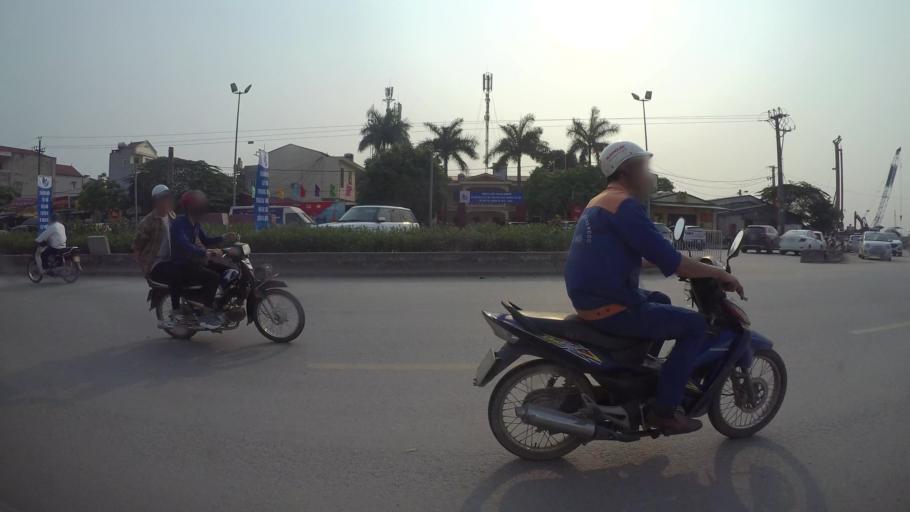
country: VN
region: Ha Noi
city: Cau Dien
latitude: 21.0060
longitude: 105.7490
